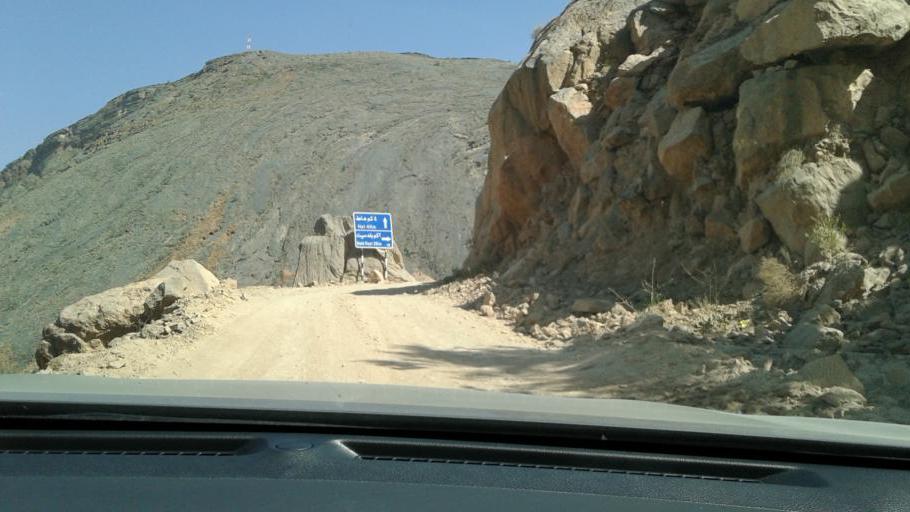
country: OM
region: Al Batinah
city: Bayt al `Awabi
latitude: 23.2045
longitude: 57.3912
